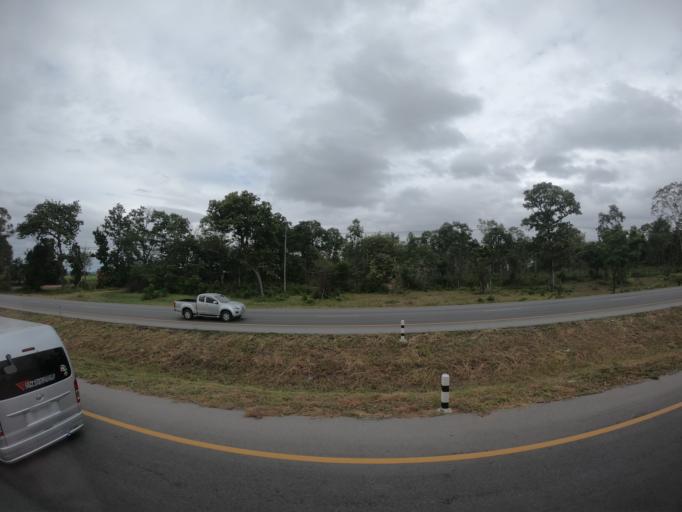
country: TH
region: Khon Kaen
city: Ban Phai
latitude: 16.0443
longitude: 102.8527
